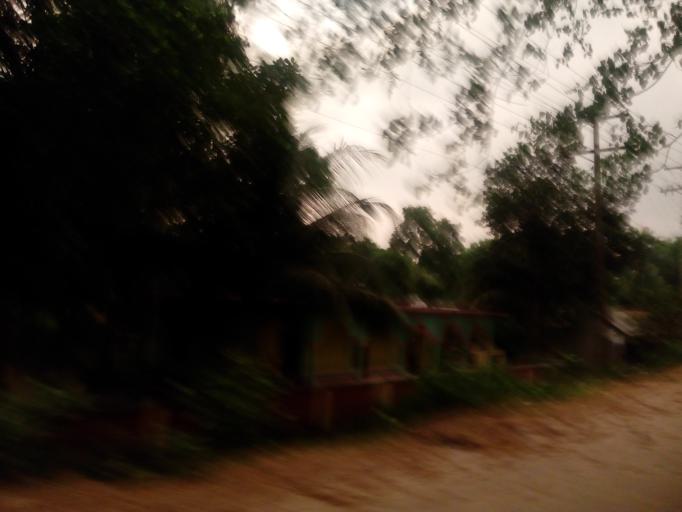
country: BD
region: Rajshahi
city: Sirajganj
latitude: 24.3019
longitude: 89.6974
